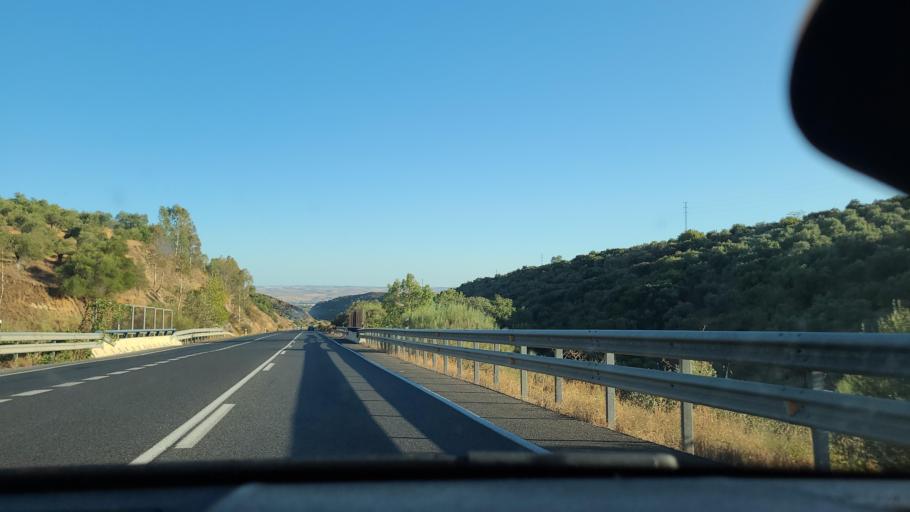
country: ES
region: Andalusia
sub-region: Province of Cordoba
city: Cordoba
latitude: 37.9622
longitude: -4.7674
